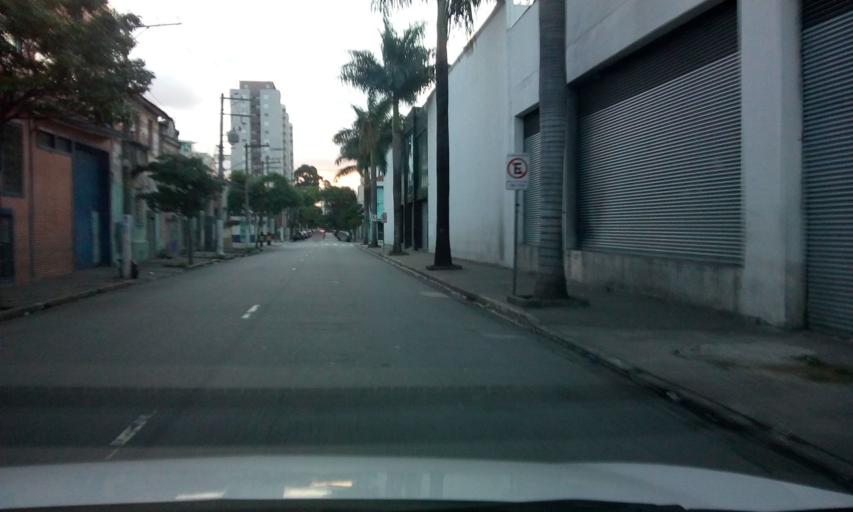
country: BR
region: Sao Paulo
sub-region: Sao Paulo
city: Sao Paulo
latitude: -23.5433
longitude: -46.6000
